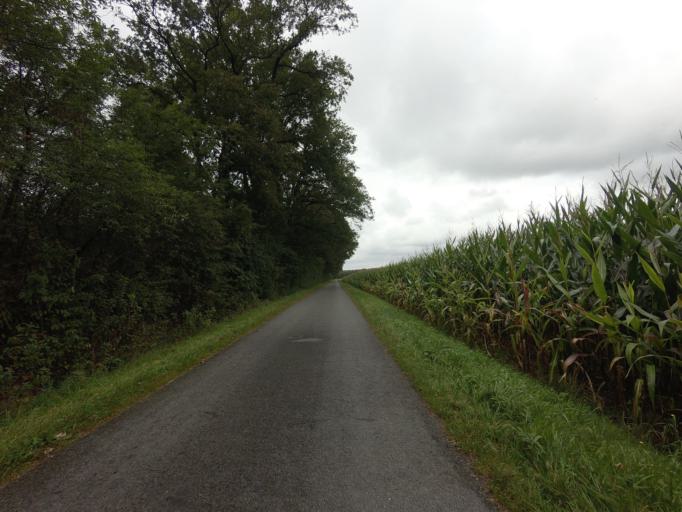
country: DE
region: North Rhine-Westphalia
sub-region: Regierungsbezirk Munster
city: Gronau
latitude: 52.2517
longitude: 7.0803
